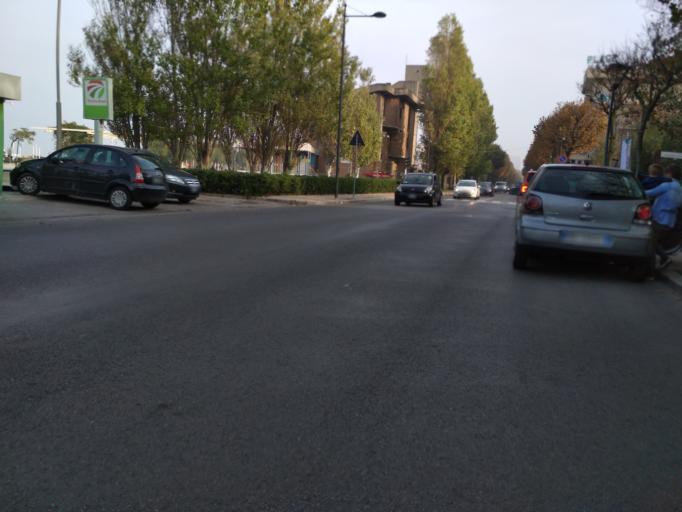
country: IT
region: Emilia-Romagna
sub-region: Provincia di Rimini
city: Rimini
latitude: 44.0781
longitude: 12.5531
